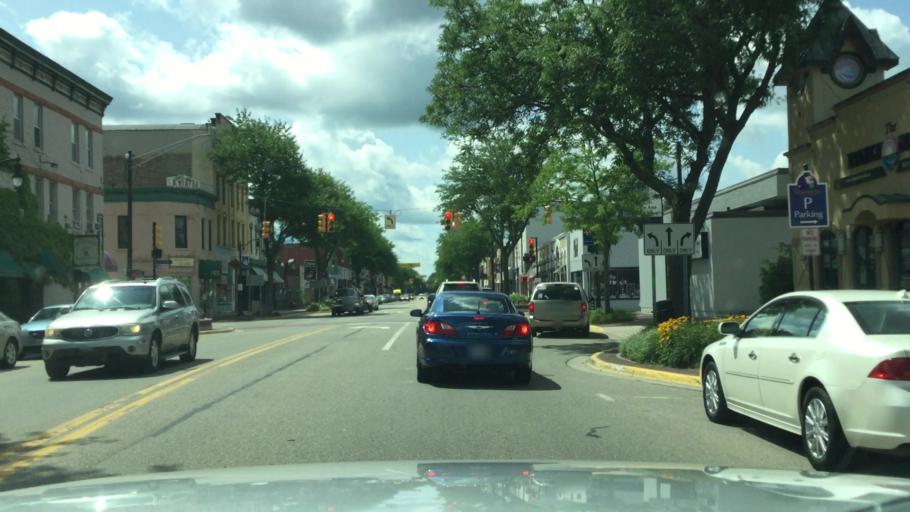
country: US
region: Michigan
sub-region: Montcalm County
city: Greenville
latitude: 43.1812
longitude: -85.2532
